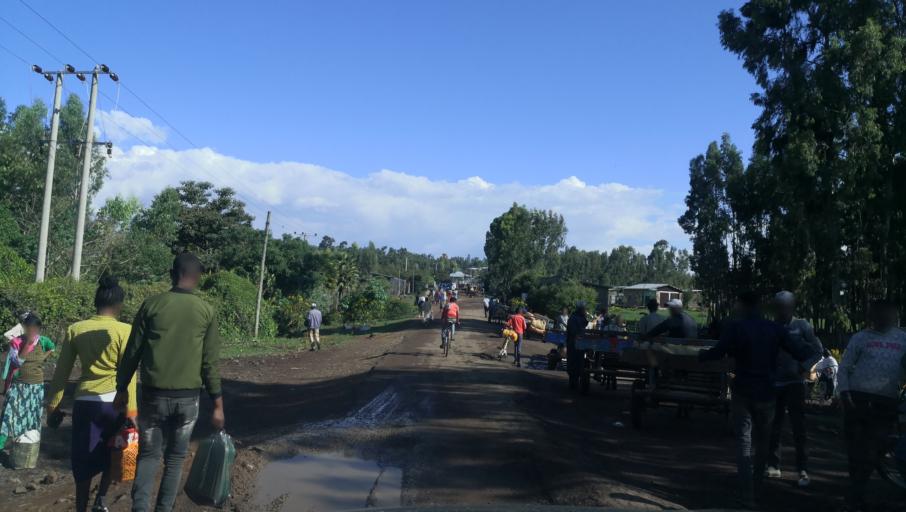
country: ET
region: Oromiya
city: Tulu Bolo
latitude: 8.6565
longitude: 38.2179
